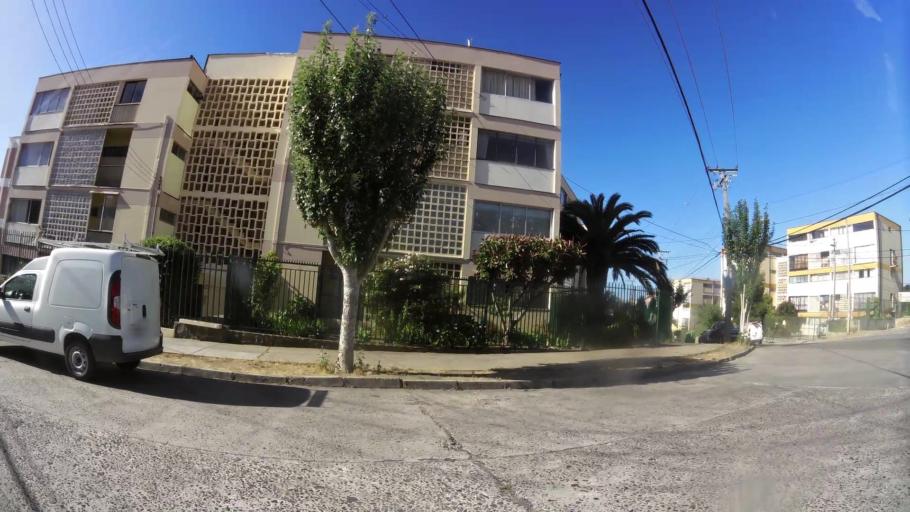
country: CL
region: Valparaiso
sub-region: Provincia de Valparaiso
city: Vina del Mar
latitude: -33.0316
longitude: -71.5581
